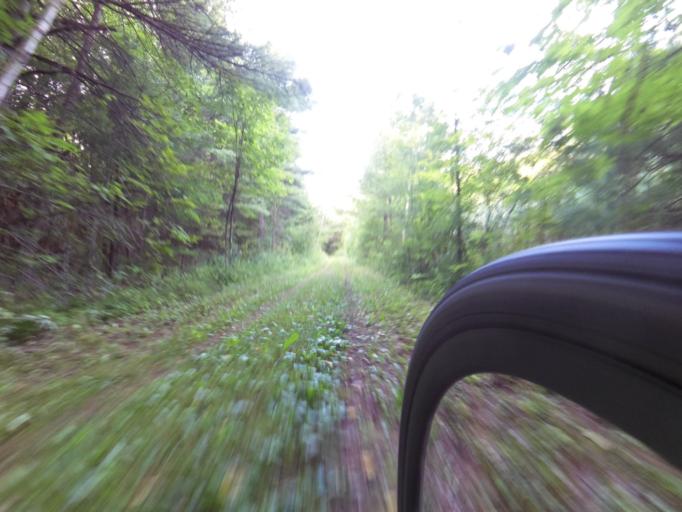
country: CA
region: Ontario
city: Gananoque
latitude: 44.5687
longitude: -76.3510
